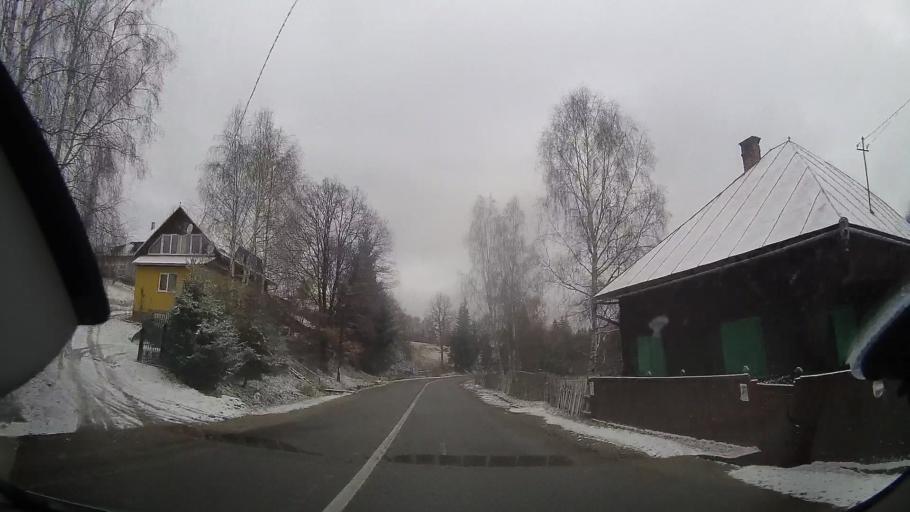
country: RO
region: Cluj
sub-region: Comuna Calatele
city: Calatele
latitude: 46.7121
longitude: 23.0416
